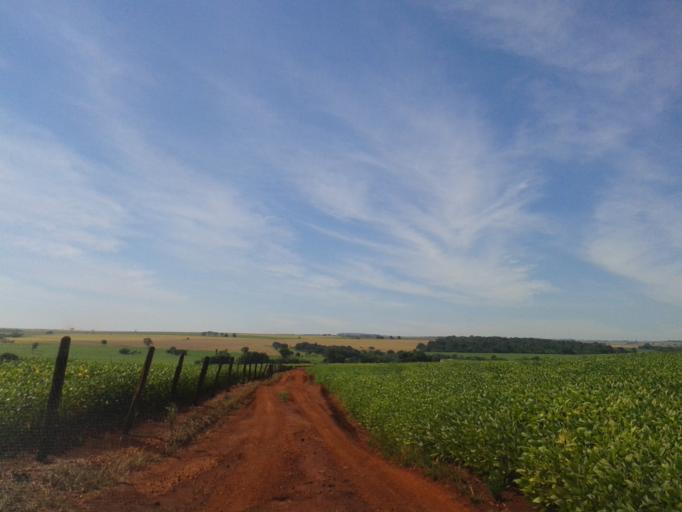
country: BR
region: Minas Gerais
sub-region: Capinopolis
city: Capinopolis
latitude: -18.6437
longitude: -49.7147
